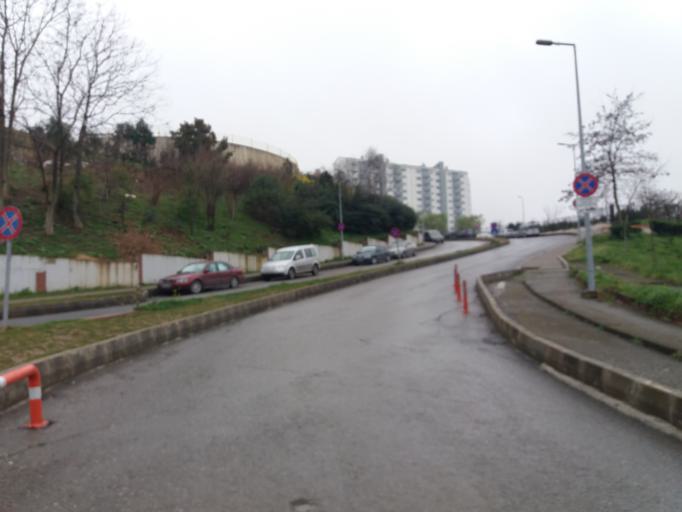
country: TR
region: Trabzon
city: Trabzon
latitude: 40.9939
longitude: 39.7678
